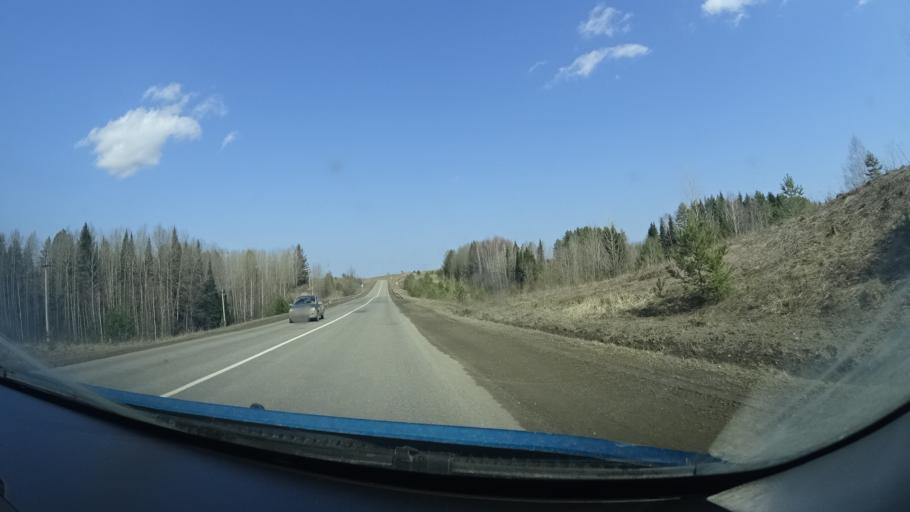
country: RU
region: Perm
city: Osa
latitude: 57.2350
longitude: 55.5944
